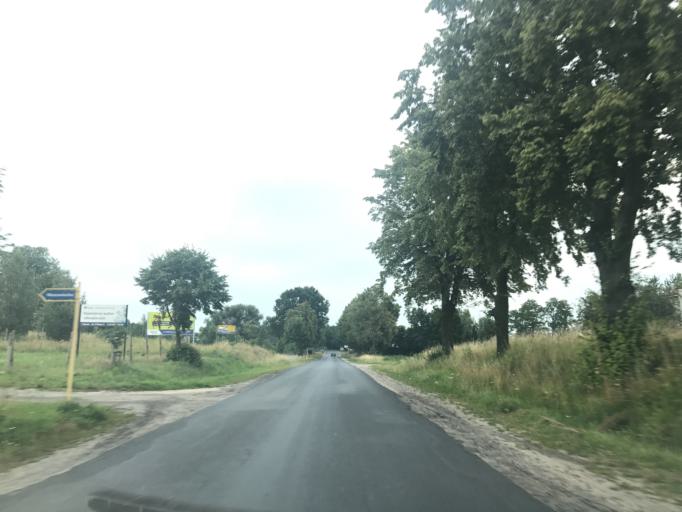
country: PL
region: Kujawsko-Pomorskie
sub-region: Powiat lipnowski
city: Lipno
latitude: 52.8320
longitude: 19.1845
